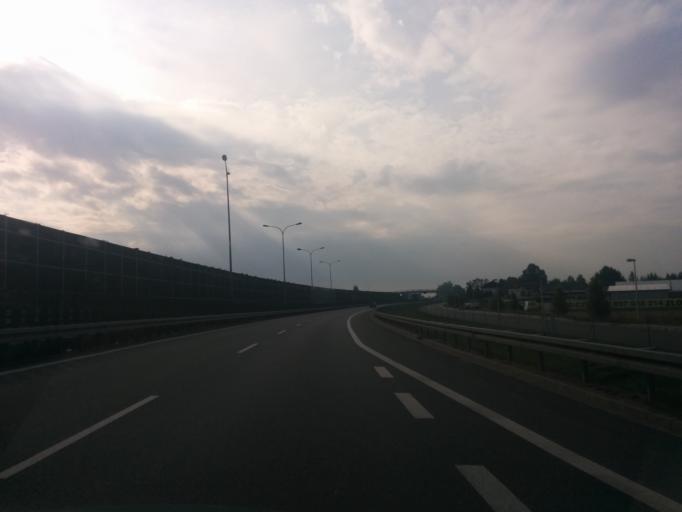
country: PL
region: Masovian Voivodeship
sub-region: Powiat bialobrzeski
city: Stara Blotnica
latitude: 51.5660
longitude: 21.0253
